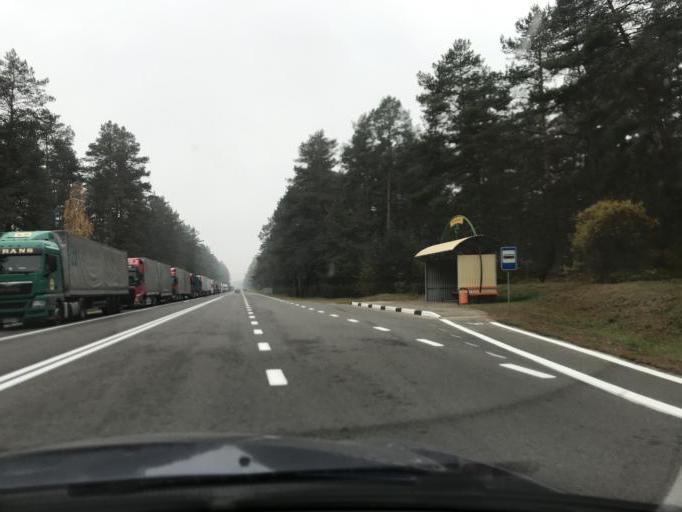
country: LT
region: Alytaus apskritis
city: Druskininkai
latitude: 53.9294
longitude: 23.9375
